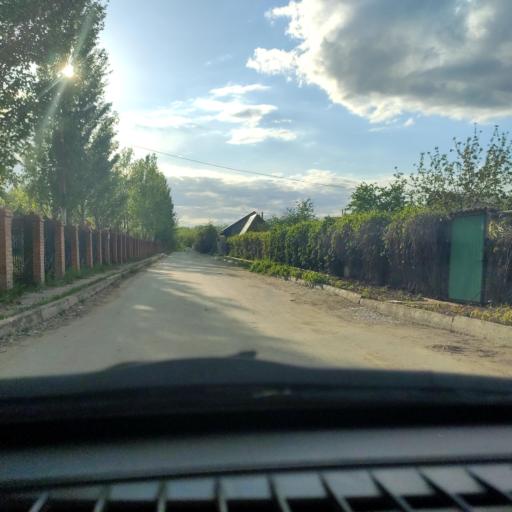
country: RU
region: Samara
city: Zhigulevsk
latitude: 53.4490
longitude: 49.5399
